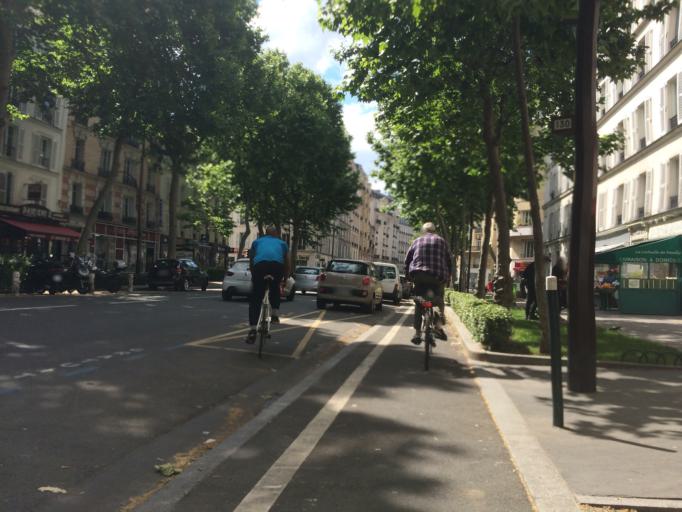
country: FR
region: Ile-de-France
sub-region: Departement des Hauts-de-Seine
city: Neuilly-sur-Seine
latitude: 48.8855
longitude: 2.2650
